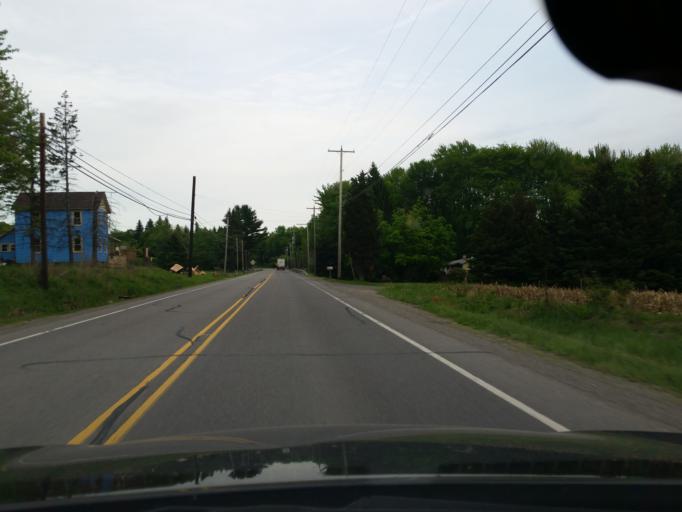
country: US
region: Pennsylvania
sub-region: Elk County
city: Ridgway
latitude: 41.4019
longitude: -78.7027
